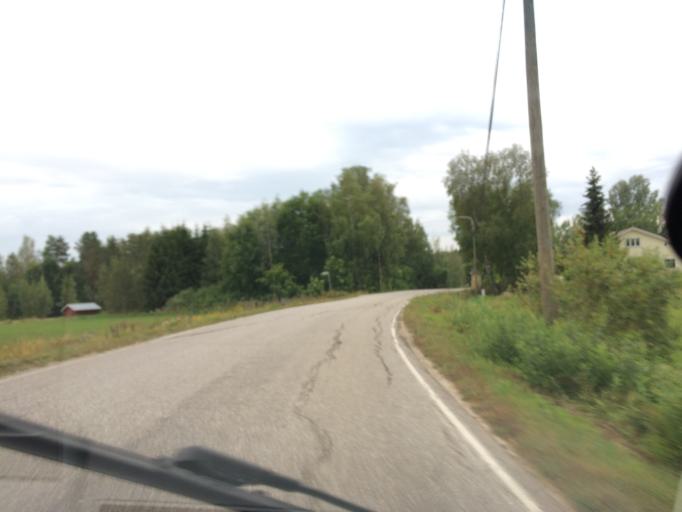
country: FI
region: Haeme
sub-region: Haemeenlinna
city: Tuulos
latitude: 61.1818
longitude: 24.7611
